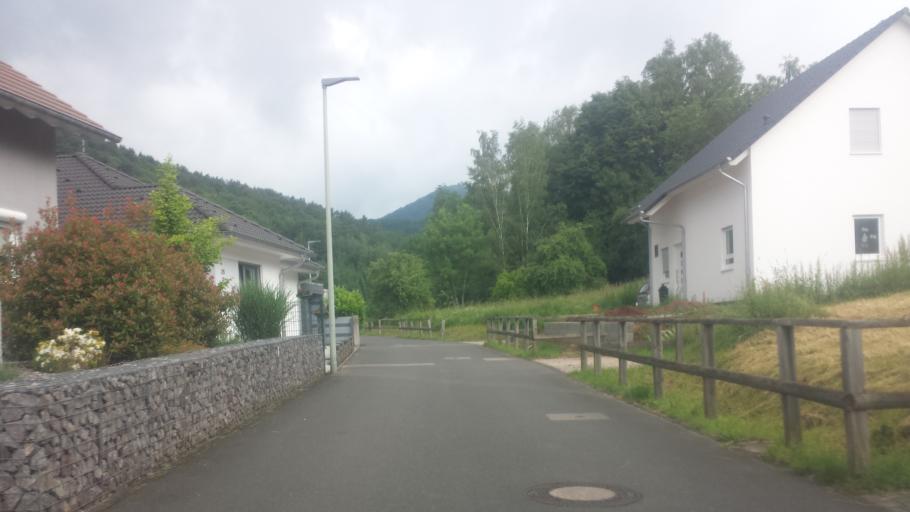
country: DE
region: Rheinland-Pfalz
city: Waldhambach
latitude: 49.1673
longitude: 7.9881
